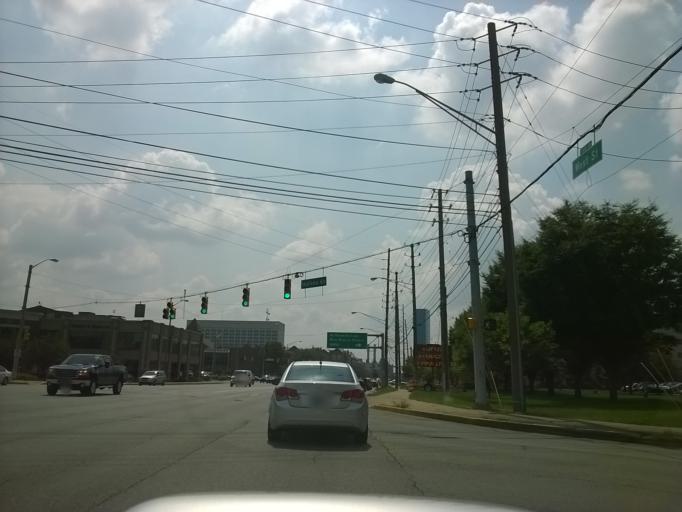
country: US
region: Indiana
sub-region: Marion County
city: Indianapolis
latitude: 39.7758
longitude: -86.1669
